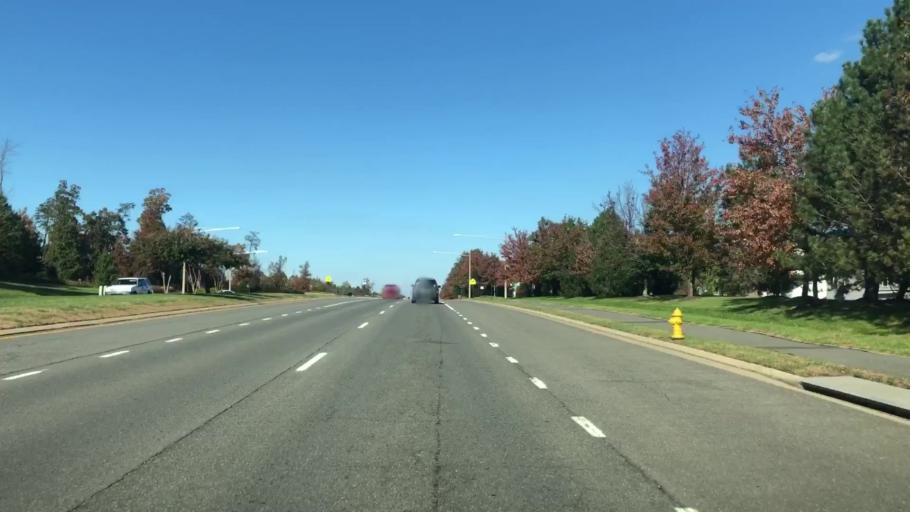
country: US
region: Virginia
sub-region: Prince William County
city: Linton Hall
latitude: 38.7359
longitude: -77.5792
